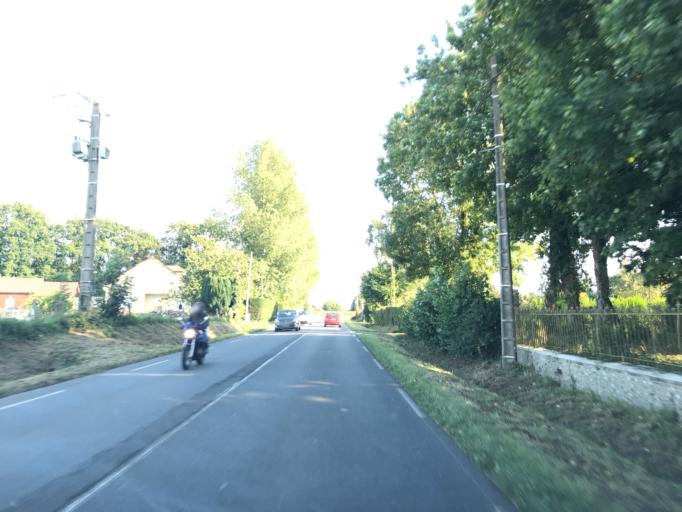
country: FR
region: Haute-Normandie
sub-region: Departement de la Seine-Maritime
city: Beuzeville-la-Grenier
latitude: 49.5996
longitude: 0.4180
